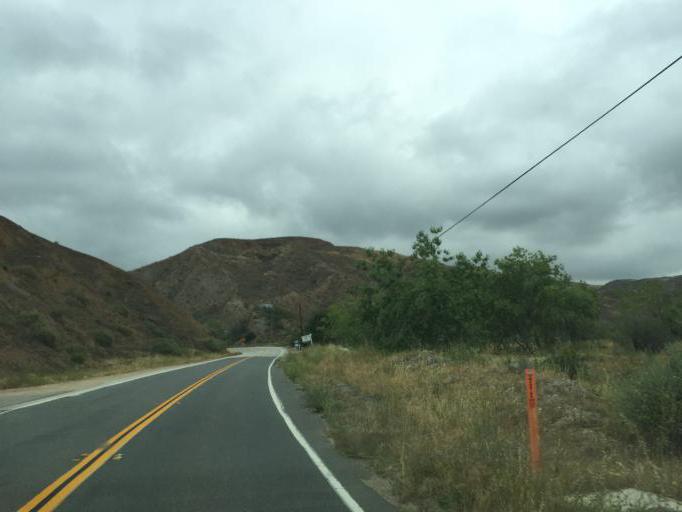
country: US
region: California
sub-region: Los Angeles County
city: Santa Clarita
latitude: 34.4926
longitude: -118.4600
